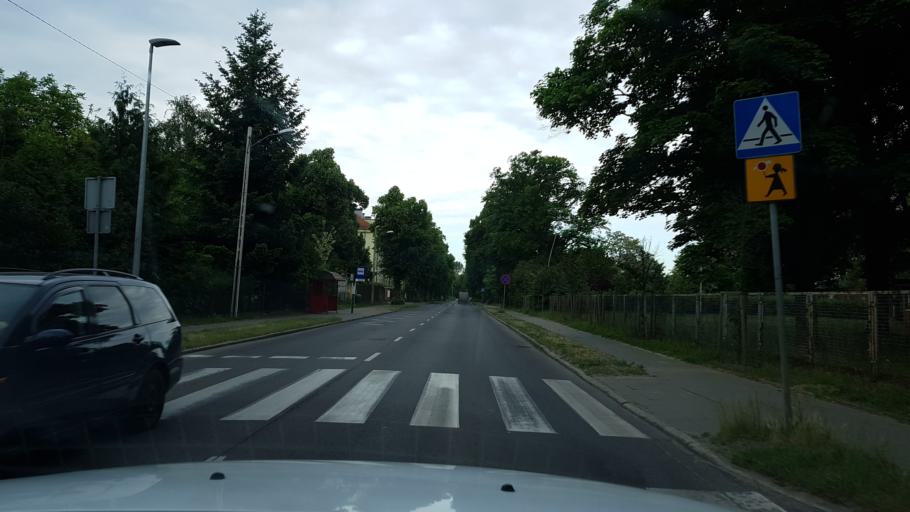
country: PL
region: West Pomeranian Voivodeship
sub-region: Szczecin
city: Szczecin
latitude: 53.3600
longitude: 14.5871
